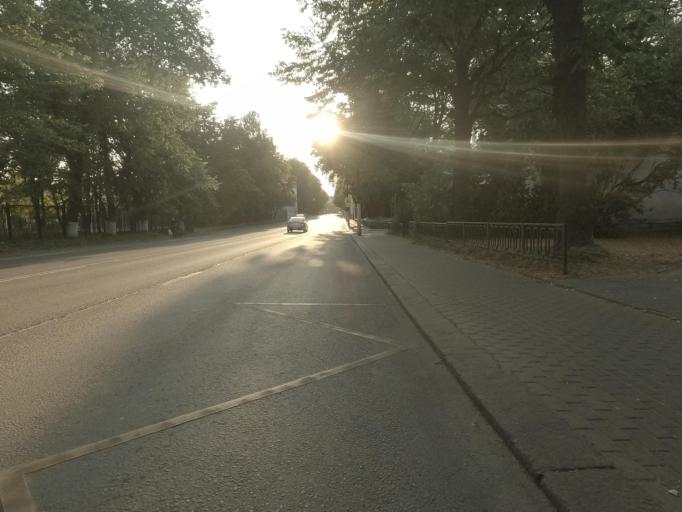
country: RU
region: Leningrad
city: Vyborg
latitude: 60.7096
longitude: 28.7654
